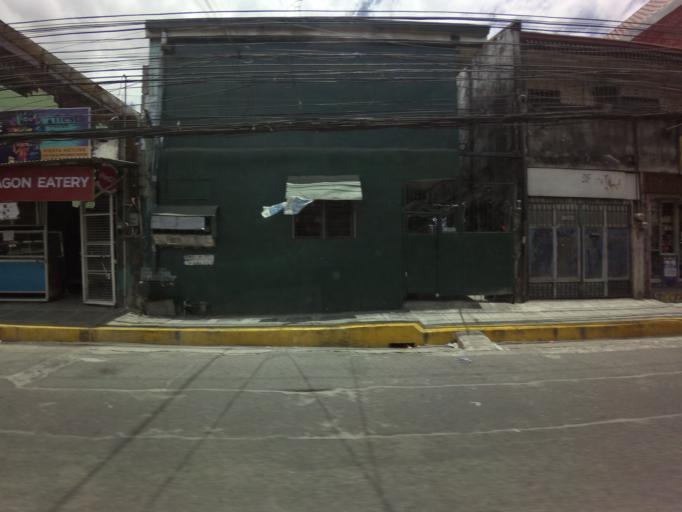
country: PH
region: Metro Manila
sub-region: Marikina
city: Calumpang
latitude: 14.6046
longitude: 121.1042
